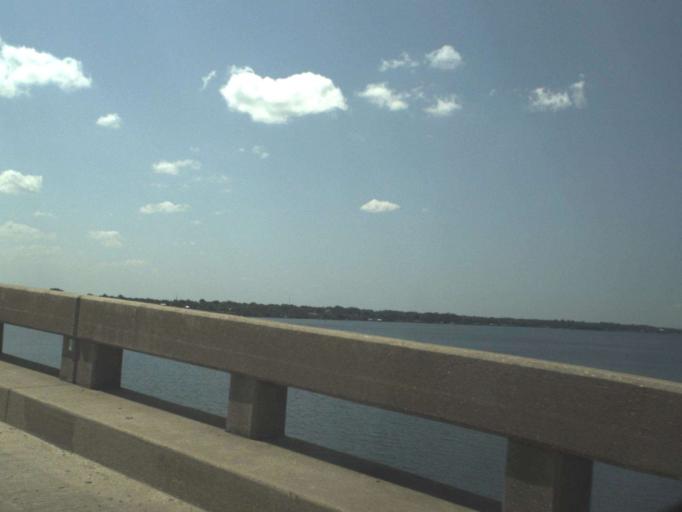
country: US
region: Florida
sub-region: Brevard County
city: Rockledge
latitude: 28.3568
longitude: -80.7156
